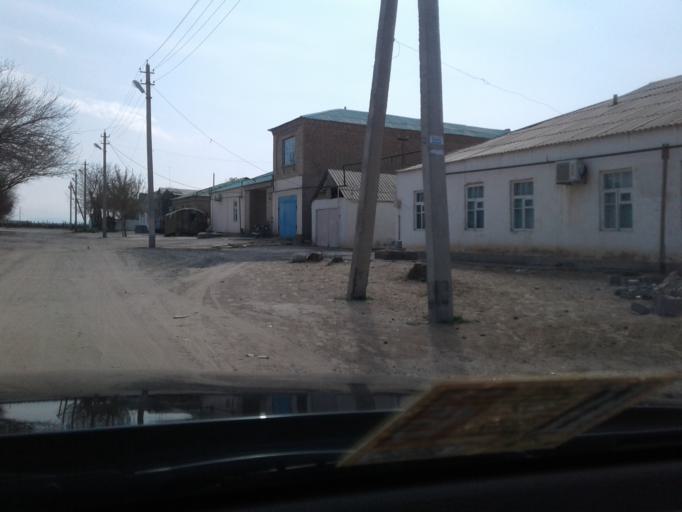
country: TM
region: Ahal
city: Abadan
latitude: 38.1189
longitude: 58.3512
